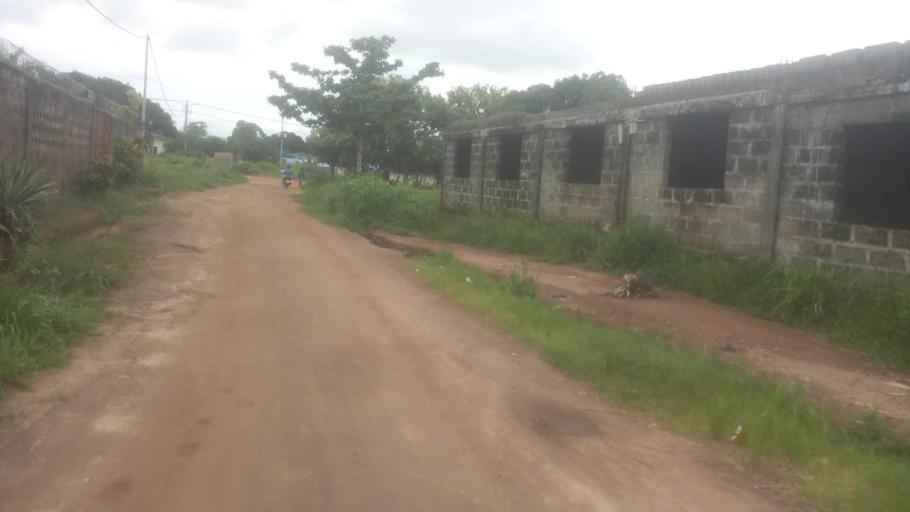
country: SL
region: Northern Province
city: Masoyila
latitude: 8.6026
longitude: -13.1897
